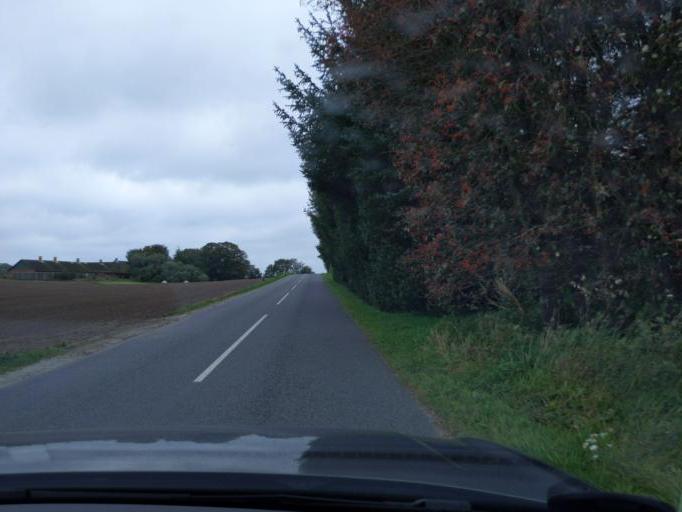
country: DK
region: North Denmark
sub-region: Mariagerfjord Kommune
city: Hobro
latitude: 56.5558
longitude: 9.6669
